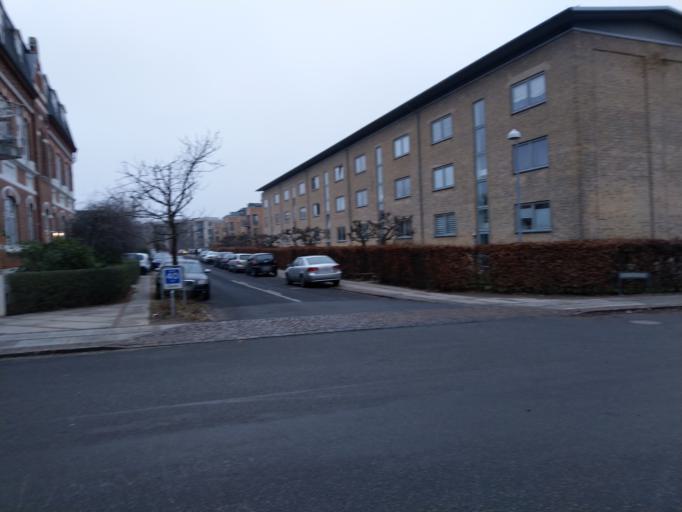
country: DK
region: Capital Region
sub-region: Lyngby-Tarbaek Kommune
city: Kongens Lyngby
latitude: 55.7700
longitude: 12.4963
